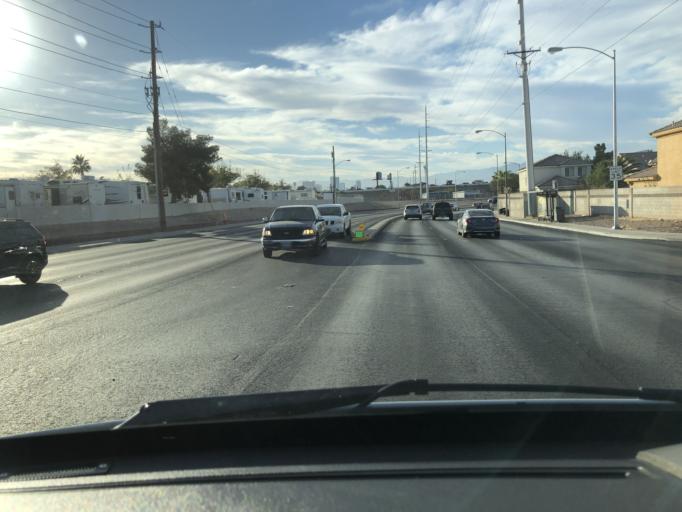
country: US
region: Nevada
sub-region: Clark County
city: Winchester
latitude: 36.1444
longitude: -115.0874
